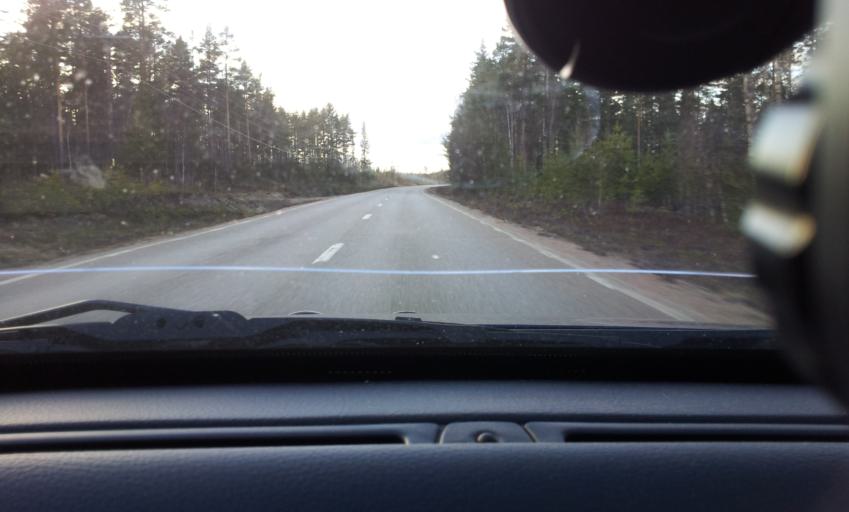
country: SE
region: Jaemtland
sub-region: Harjedalens Kommun
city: Sveg
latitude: 62.0999
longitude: 15.0744
